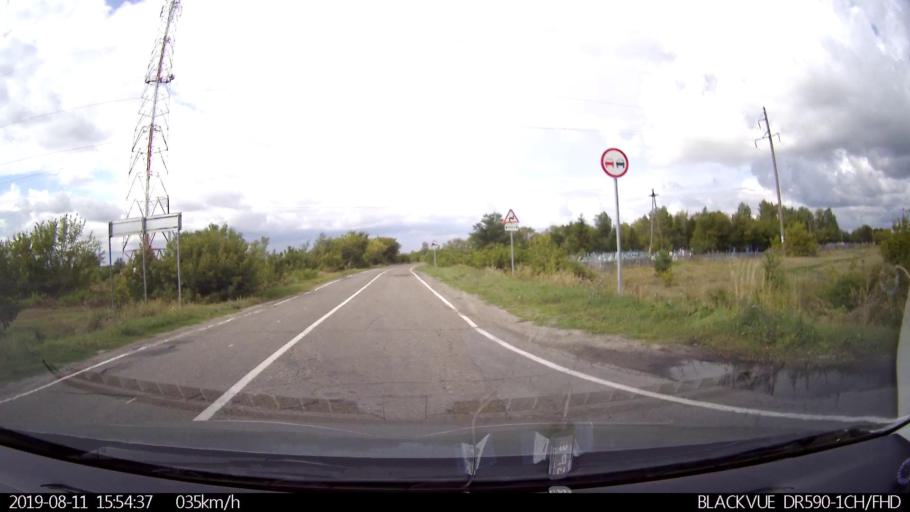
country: RU
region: Ulyanovsk
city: Ignatovka
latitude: 53.9421
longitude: 47.6562
